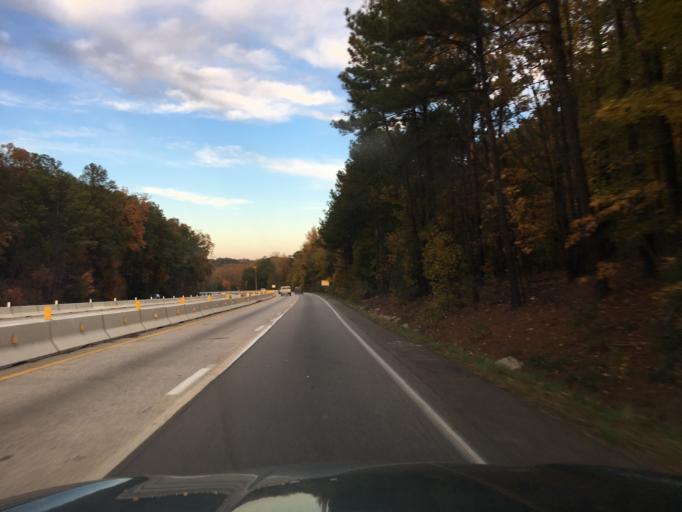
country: US
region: South Carolina
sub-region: Lexington County
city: Oak Grove
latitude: 33.9931
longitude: -81.1809
